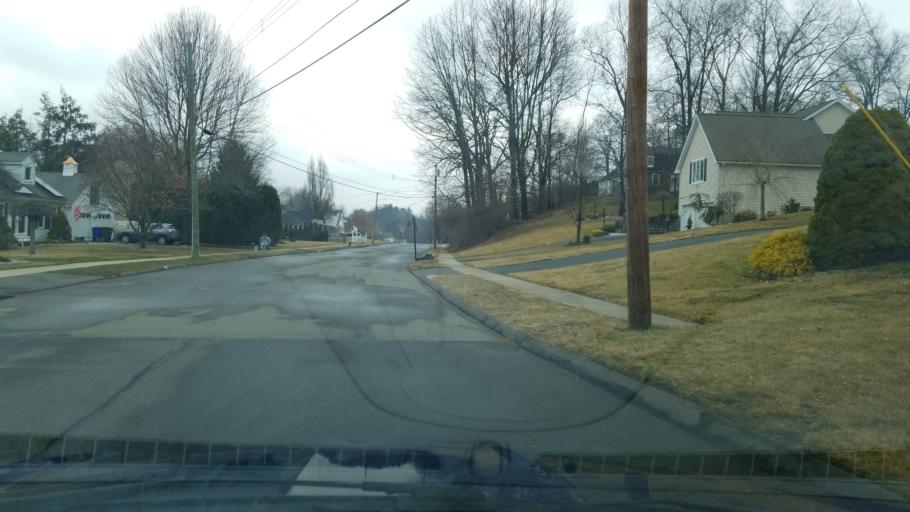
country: US
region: Connecticut
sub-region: Hartford County
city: Wethersfield
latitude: 41.6846
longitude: -72.6676
